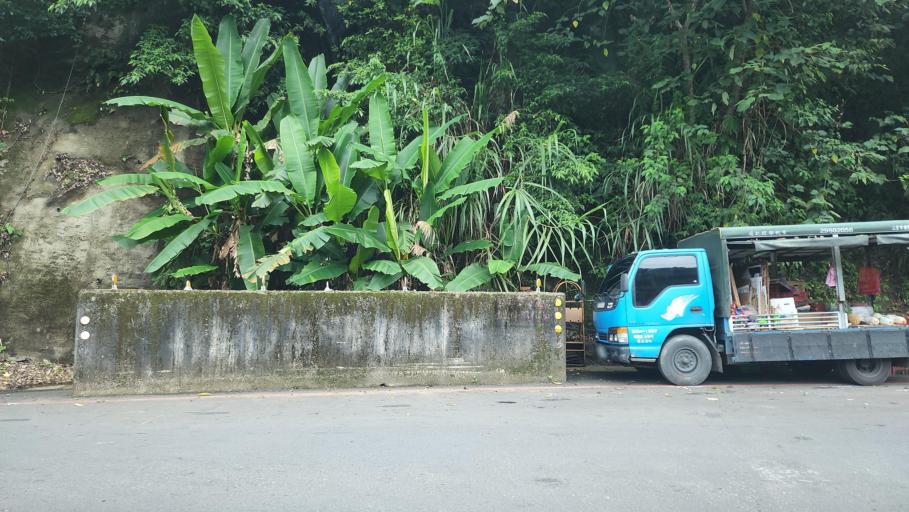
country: TW
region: Taiwan
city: Daxi
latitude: 24.8746
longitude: 121.3908
